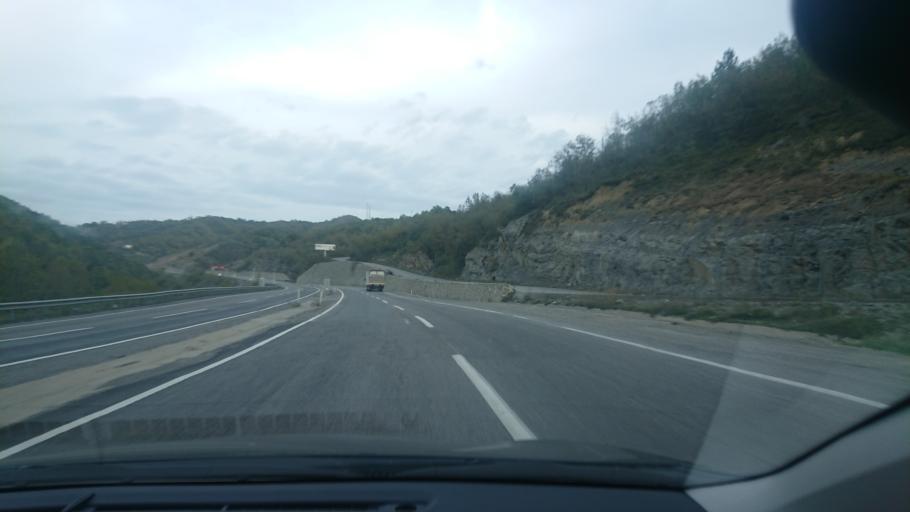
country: TR
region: Zonguldak
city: Beycuma
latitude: 41.4063
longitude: 31.9358
